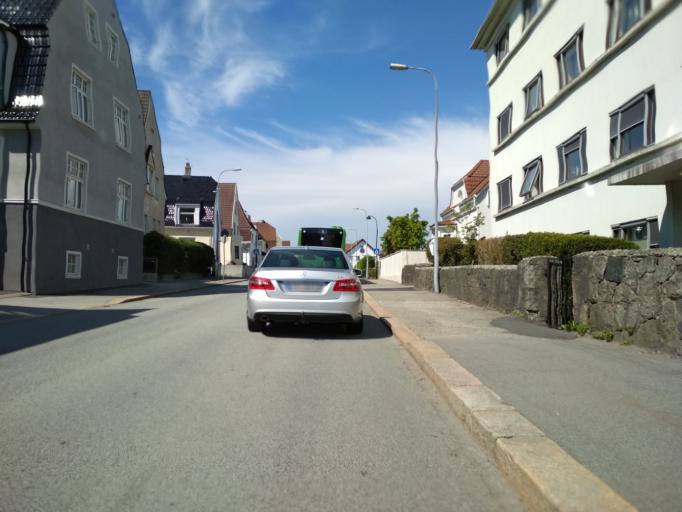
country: NO
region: Rogaland
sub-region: Stavanger
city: Stavanger
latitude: 58.9678
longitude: 5.7236
